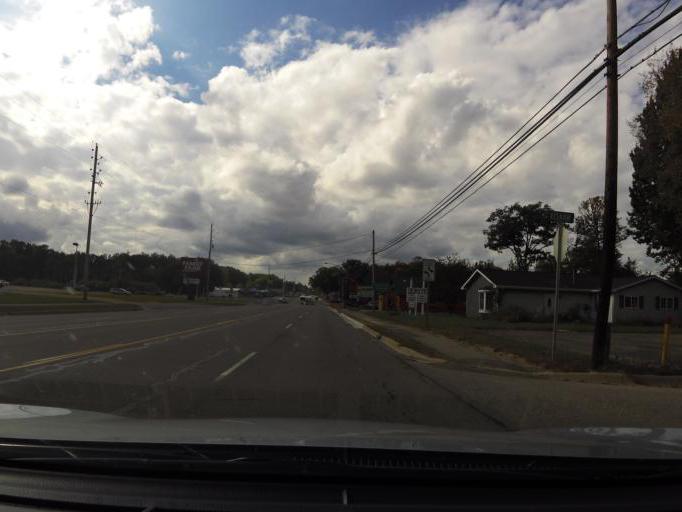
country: US
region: Michigan
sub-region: Roscommon County
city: Houghton Lake
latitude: 44.2986
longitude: -84.7097
